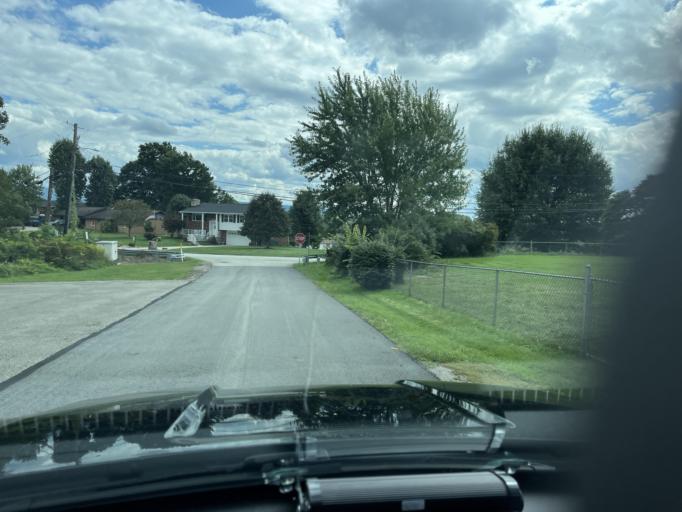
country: US
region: Pennsylvania
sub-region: Fayette County
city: South Uniontown
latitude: 39.8985
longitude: -79.7606
